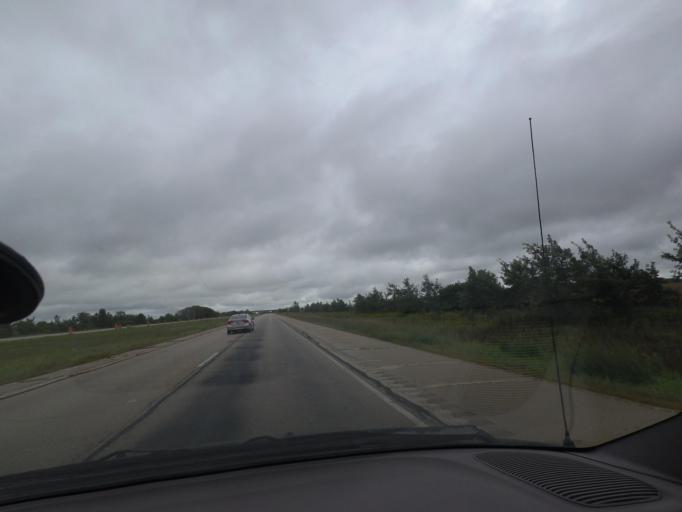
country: US
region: Illinois
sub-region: Piatt County
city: Cerro Gordo
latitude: 40.0174
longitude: -88.7342
